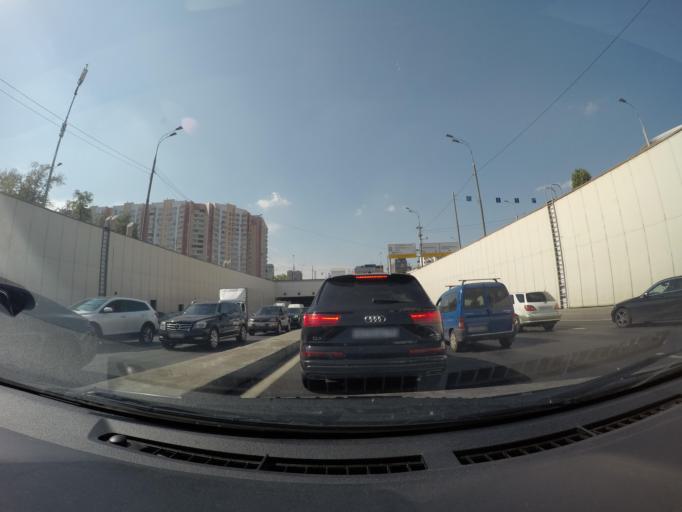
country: RU
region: Moscow
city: Mar'ina Roshcha
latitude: 55.7931
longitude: 37.6183
